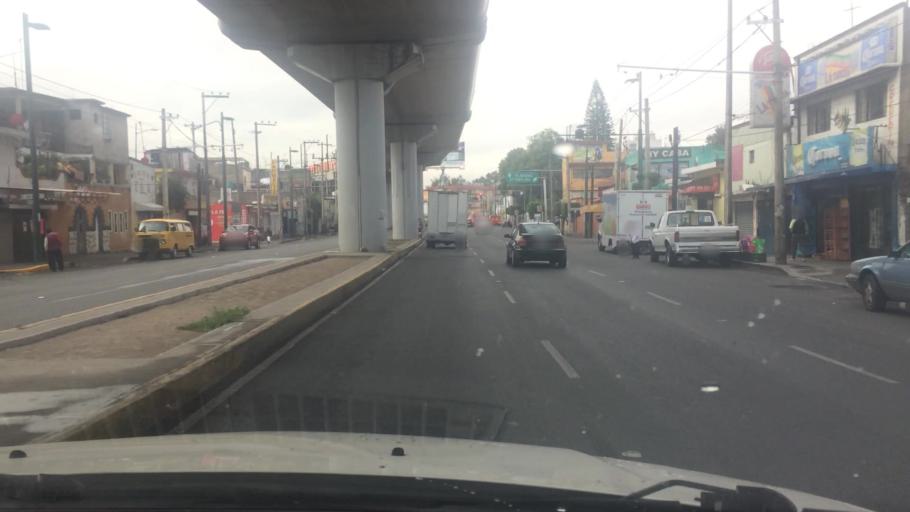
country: MX
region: Mexico City
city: Iztapalapa
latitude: 19.3312
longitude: -99.1076
